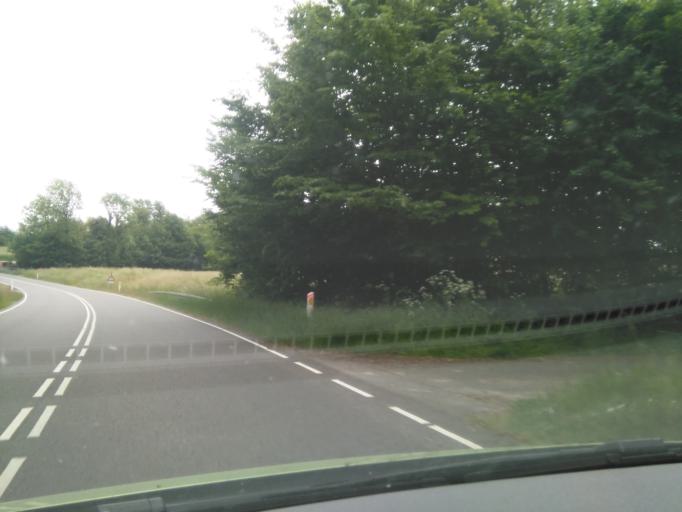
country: DK
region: Capital Region
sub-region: Bornholm Kommune
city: Akirkeby
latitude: 55.2309
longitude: 14.8775
